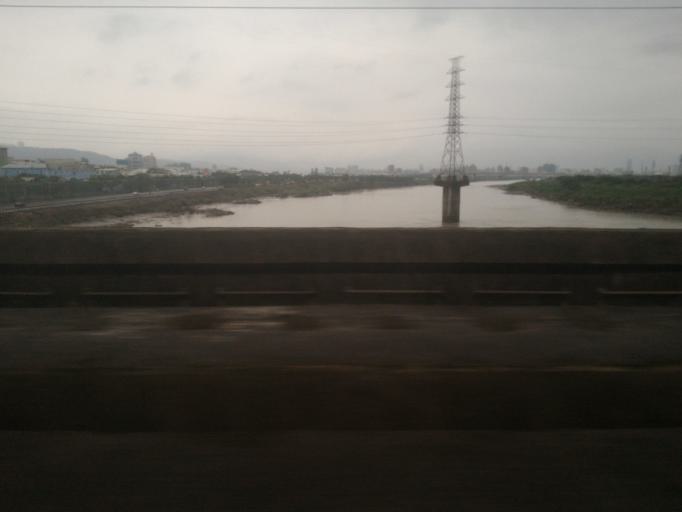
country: TW
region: Taipei
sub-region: Taipei
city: Banqiao
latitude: 25.0049
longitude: 121.4371
